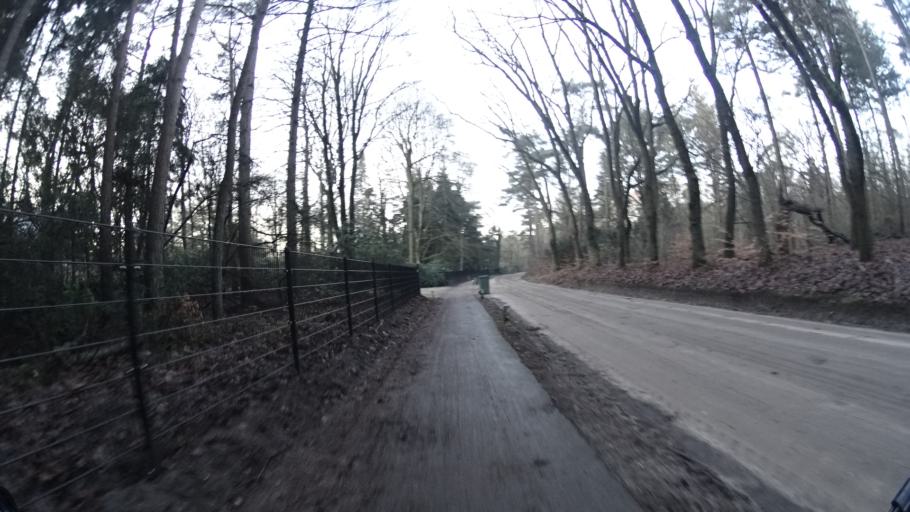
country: NL
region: Gelderland
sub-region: Gemeente Ede
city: Lunteren
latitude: 52.0866
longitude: 5.6594
